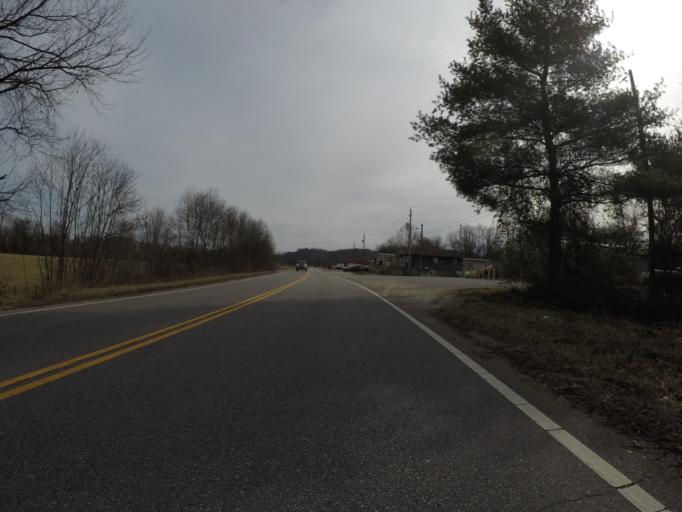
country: US
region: West Virginia
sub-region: Cabell County
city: Pea Ridge
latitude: 38.4416
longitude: -82.3740
